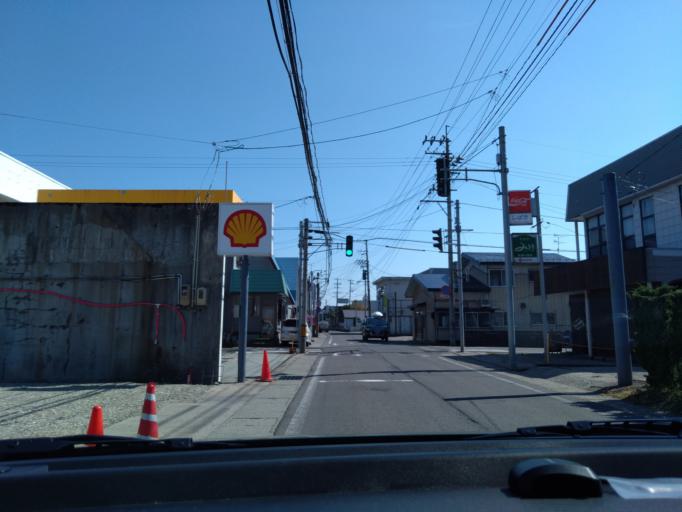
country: JP
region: Akita
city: Kakunodatemachi
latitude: 39.5014
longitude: 140.5944
